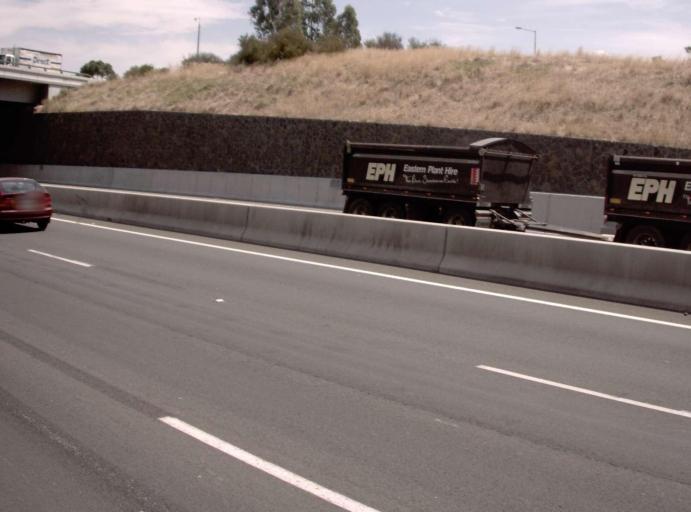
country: AU
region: Victoria
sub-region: Moonee Valley
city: Keilor East
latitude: -37.7271
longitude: 144.8608
